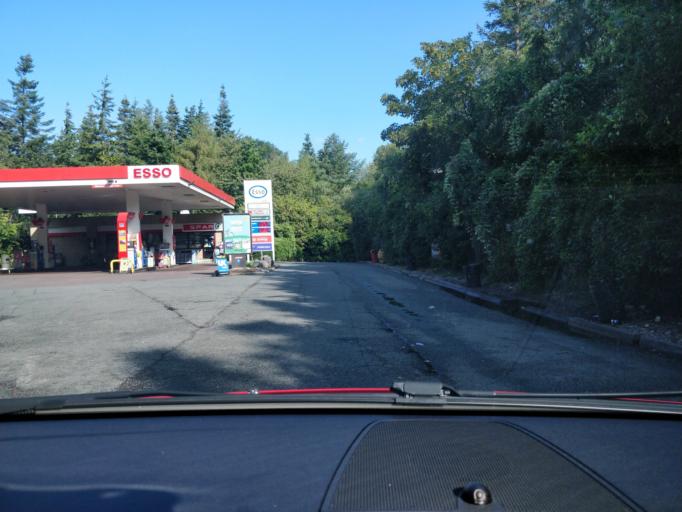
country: GB
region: Wales
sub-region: Denbighshire
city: Bodelwyddan
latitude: 53.2682
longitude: -3.5185
